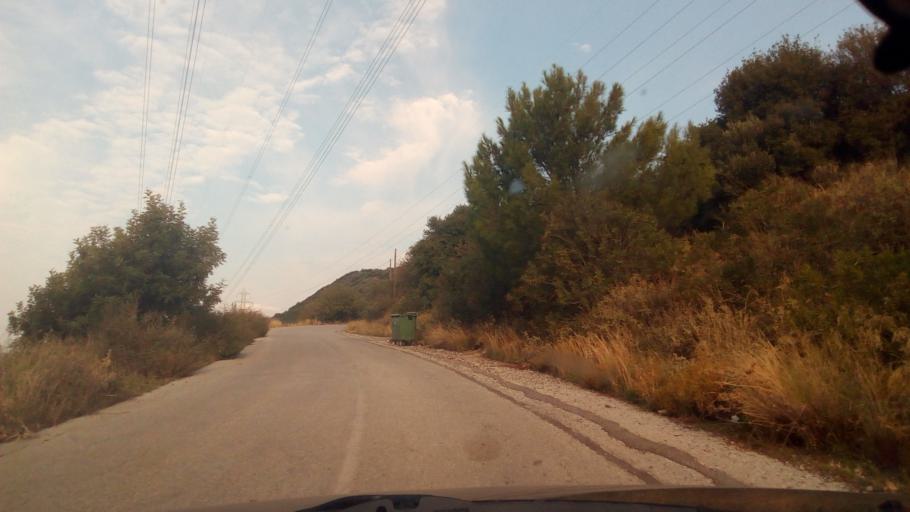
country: GR
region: West Greece
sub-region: Nomos Aitolias kai Akarnanias
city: Nafpaktos
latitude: 38.4132
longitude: 21.9268
